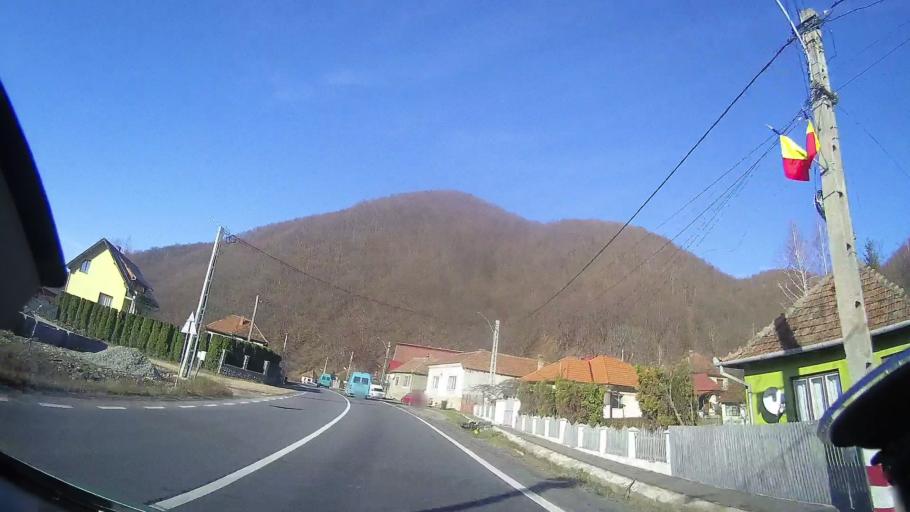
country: RO
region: Cluj
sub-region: Comuna Ciucea
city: Ciucea
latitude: 46.9575
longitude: 22.8094
